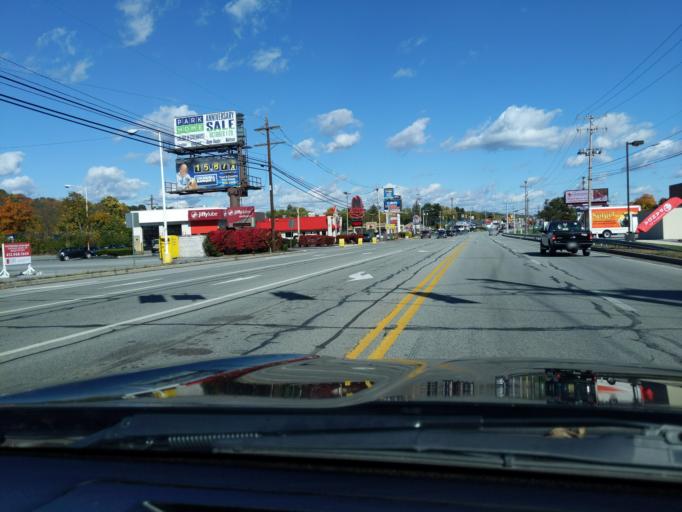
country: US
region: Pennsylvania
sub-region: Blair County
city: Lakemont
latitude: 40.4712
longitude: -78.4065
